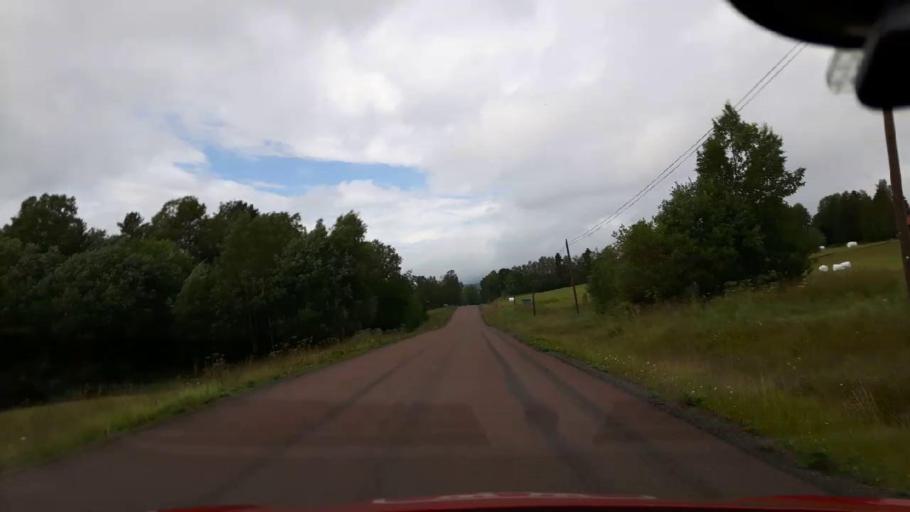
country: SE
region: Jaemtland
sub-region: Krokoms Kommun
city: Valla
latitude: 63.3690
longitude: 14.0436
